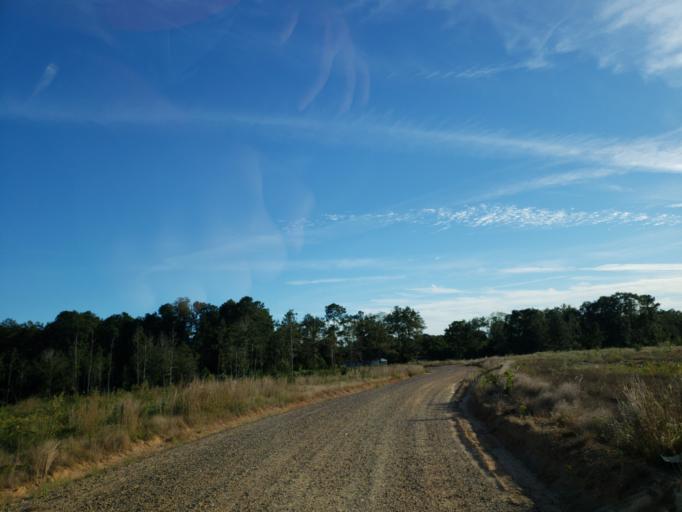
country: US
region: Mississippi
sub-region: Perry County
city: Richton
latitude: 31.3446
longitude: -88.7987
